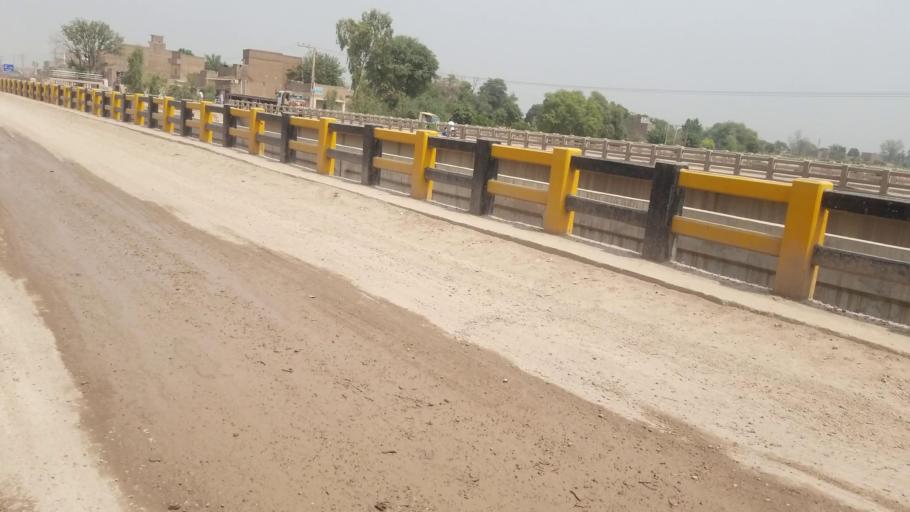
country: PK
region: Khyber Pakhtunkhwa
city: Peshawar
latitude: 33.9630
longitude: 71.5421
